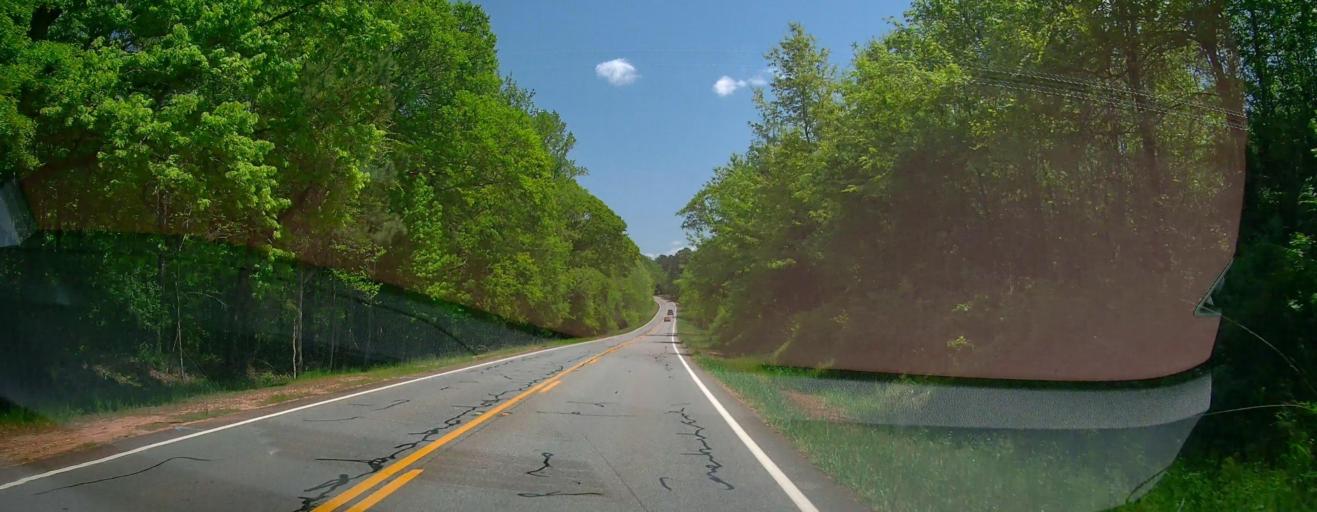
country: US
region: Georgia
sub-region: Jasper County
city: Monticello
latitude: 33.3154
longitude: -83.7122
